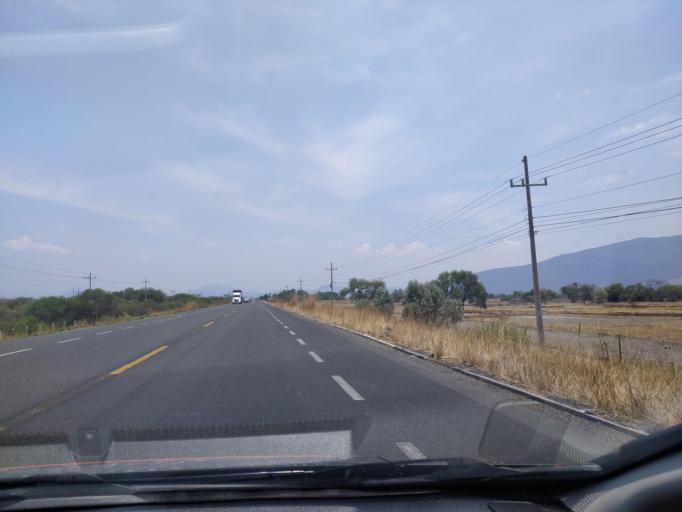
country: MX
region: Jalisco
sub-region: Acatlan de Juarez
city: Villa de los Ninos
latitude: 20.3295
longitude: -103.5905
